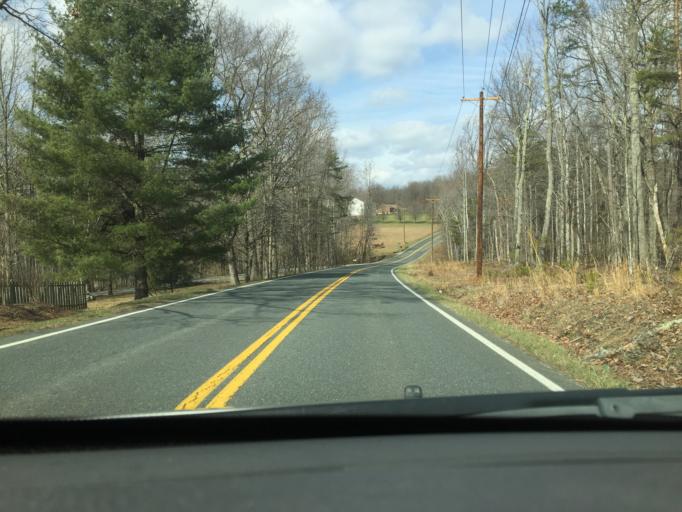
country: US
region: Virginia
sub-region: City of Lynchburg
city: West Lynchburg
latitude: 37.3296
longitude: -79.1650
